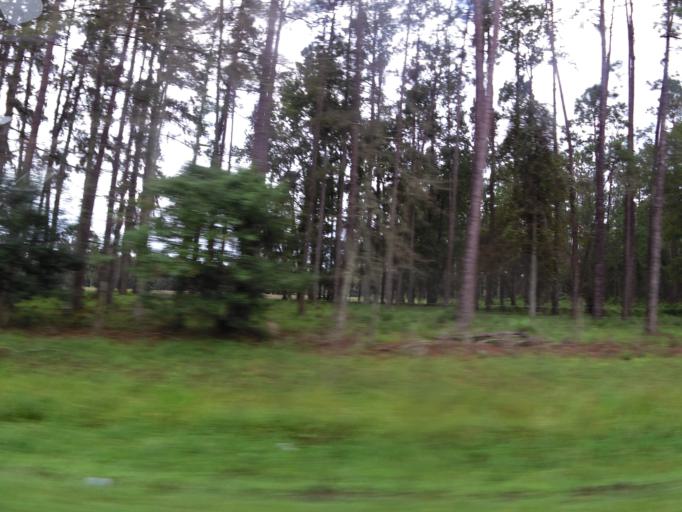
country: US
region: Florida
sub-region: Duval County
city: Baldwin
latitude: 30.4004
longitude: -81.9875
